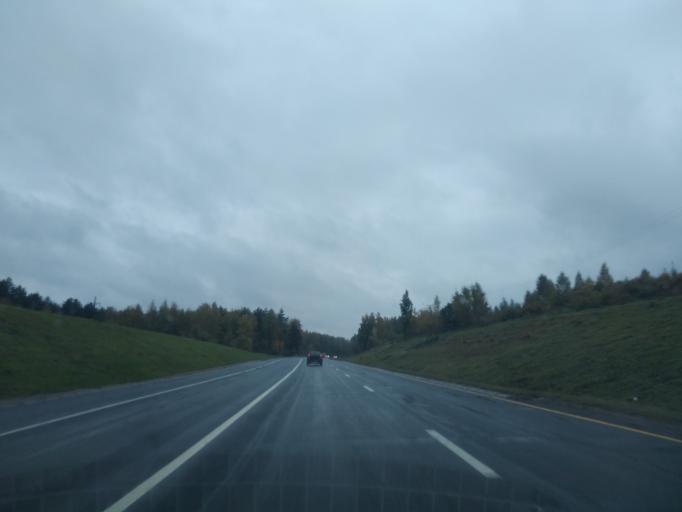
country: RU
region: Tula
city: Barsuki
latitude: 54.2930
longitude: 37.5357
